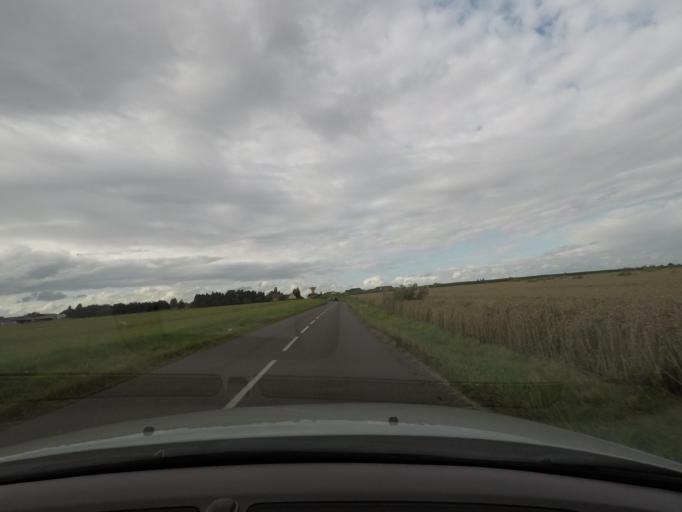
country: FR
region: Haute-Normandie
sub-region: Departement de la Seine-Maritime
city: Ymare
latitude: 49.3481
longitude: 1.1843
